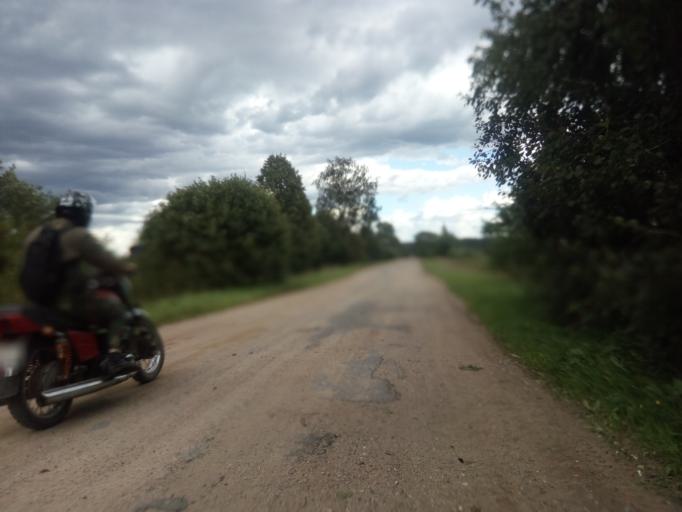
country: BY
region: Vitebsk
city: Dzisna
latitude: 55.7092
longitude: 28.3050
